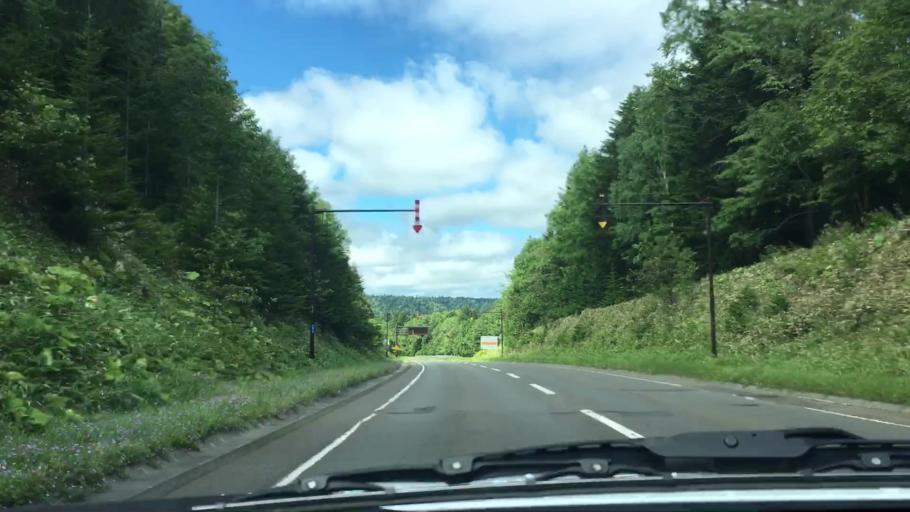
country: JP
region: Hokkaido
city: Bihoro
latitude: 43.4465
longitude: 144.0328
